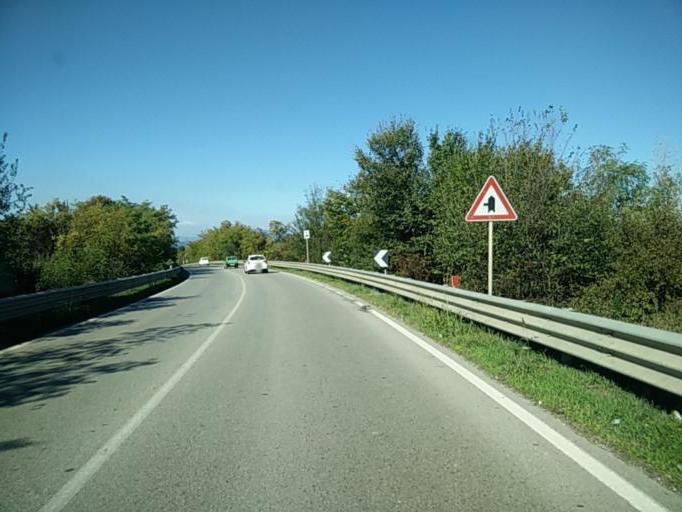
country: IT
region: Lombardy
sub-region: Provincia di Brescia
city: San Martino della Battaglia
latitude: 45.4364
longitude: 10.6062
